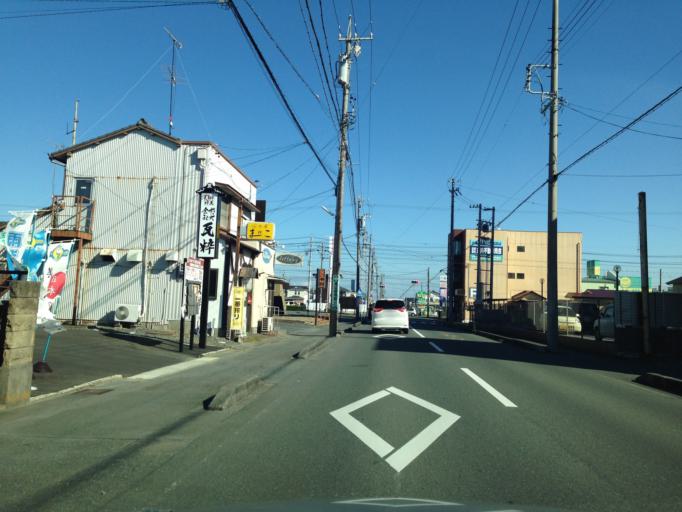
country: JP
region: Shizuoka
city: Fukuroi
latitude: 34.7531
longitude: 137.9188
